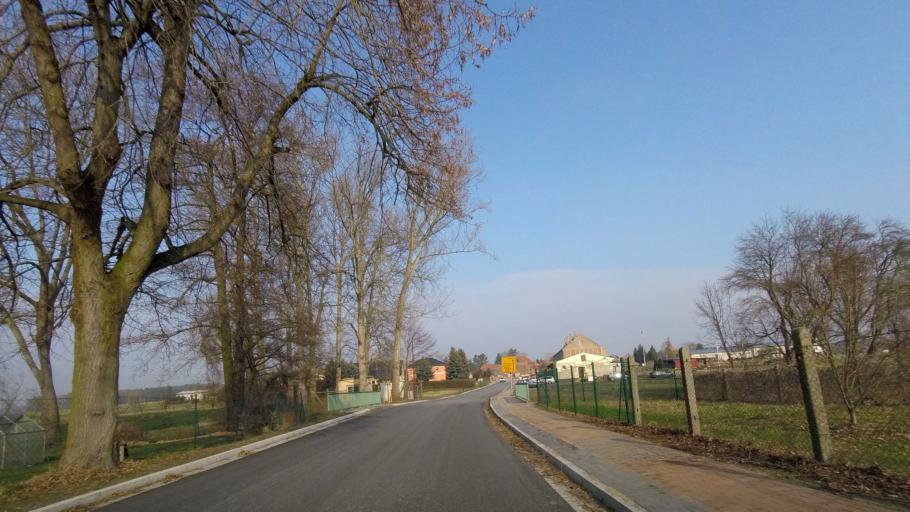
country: DE
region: Brandenburg
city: Juterbog
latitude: 51.9643
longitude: 13.0436
